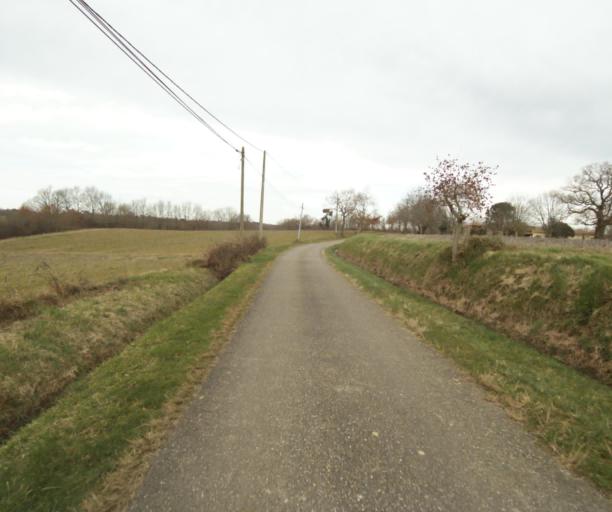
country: FR
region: Aquitaine
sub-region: Departement des Landes
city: Gabarret
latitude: 43.9236
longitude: 0.0336
